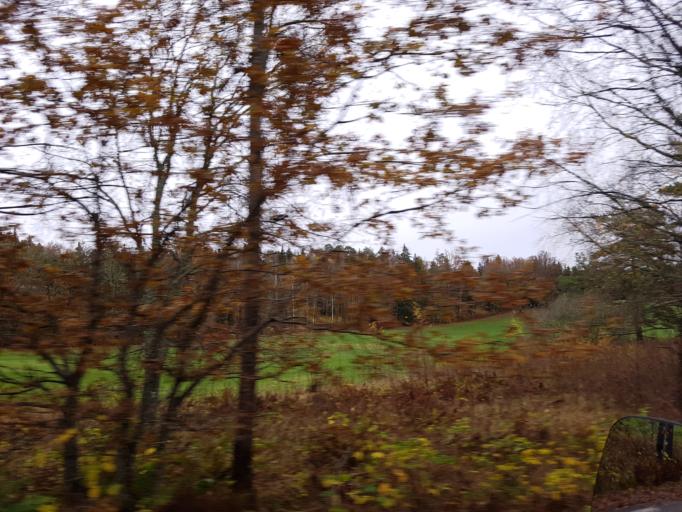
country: SE
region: Vaestra Goetaland
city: Svanesund
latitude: 58.2057
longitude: 11.8060
